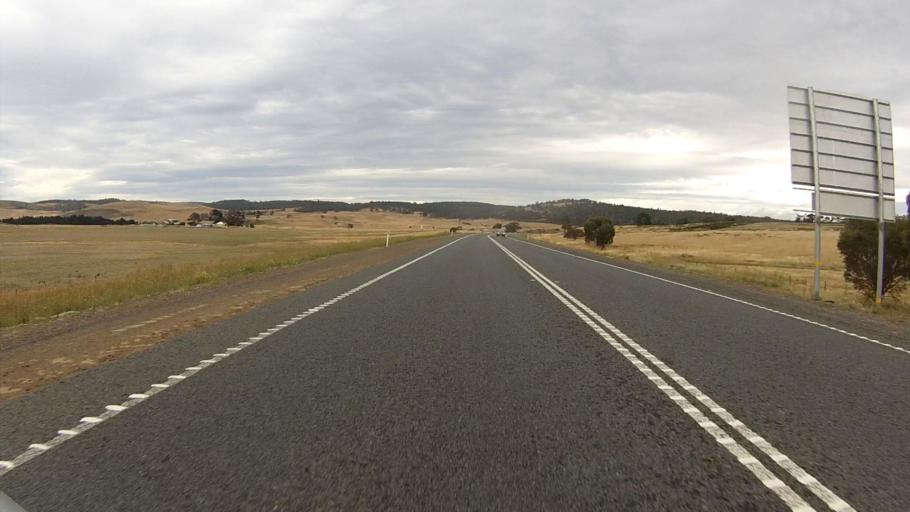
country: AU
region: Tasmania
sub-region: Brighton
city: Bridgewater
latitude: -42.3061
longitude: 147.3578
